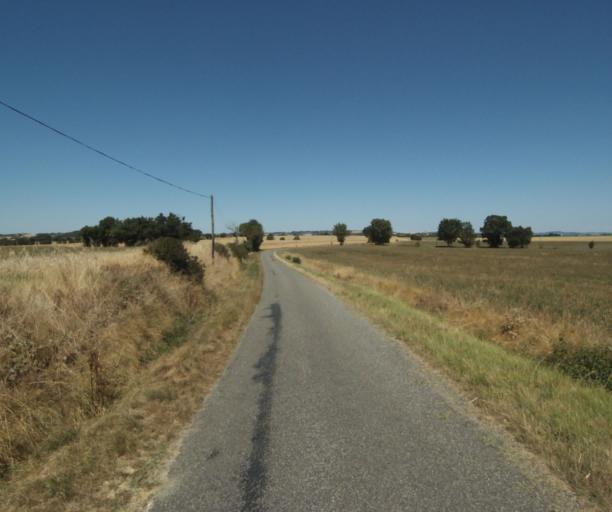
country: FR
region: Midi-Pyrenees
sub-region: Departement de la Haute-Garonne
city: Saint-Felix-Lauragais
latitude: 43.4669
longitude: 1.9091
